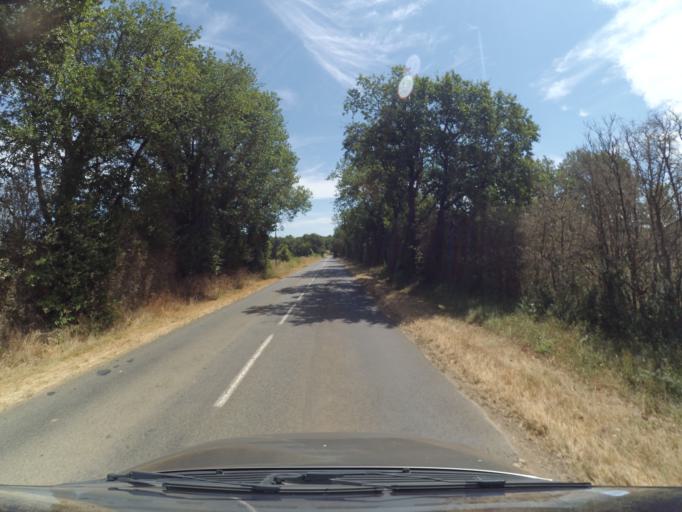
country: FR
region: Poitou-Charentes
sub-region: Departement de la Vienne
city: Vivonne
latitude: 46.4149
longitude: 0.3235
